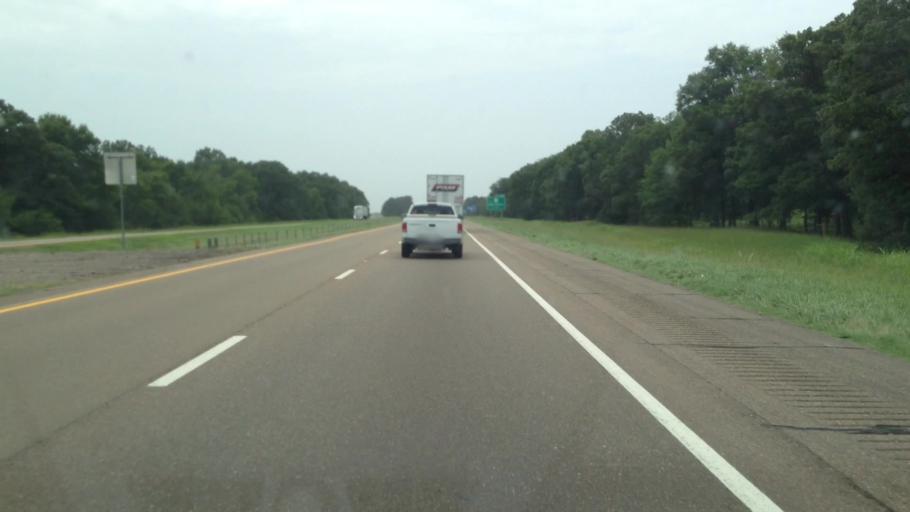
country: US
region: Texas
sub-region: Bowie County
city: New Boston
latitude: 33.4724
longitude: -94.3851
